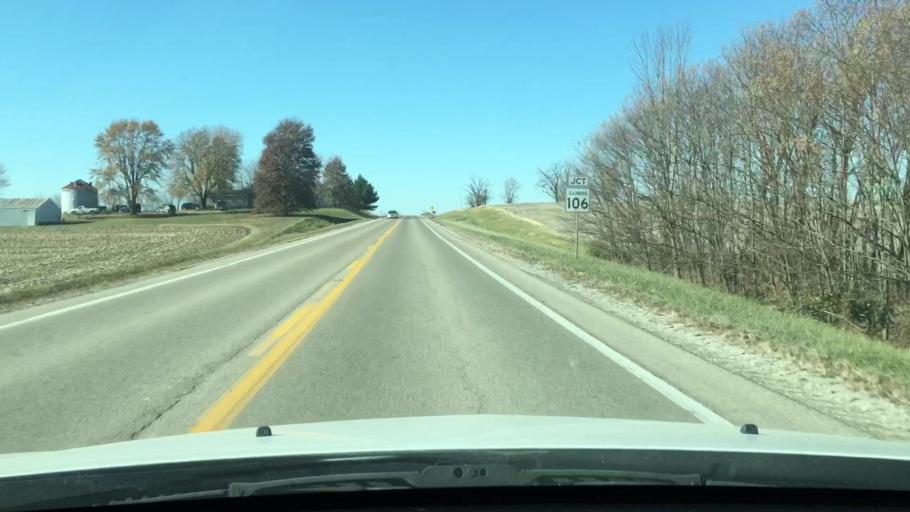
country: US
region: Illinois
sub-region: Pike County
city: Pittsfield
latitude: 39.6051
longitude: -90.8678
